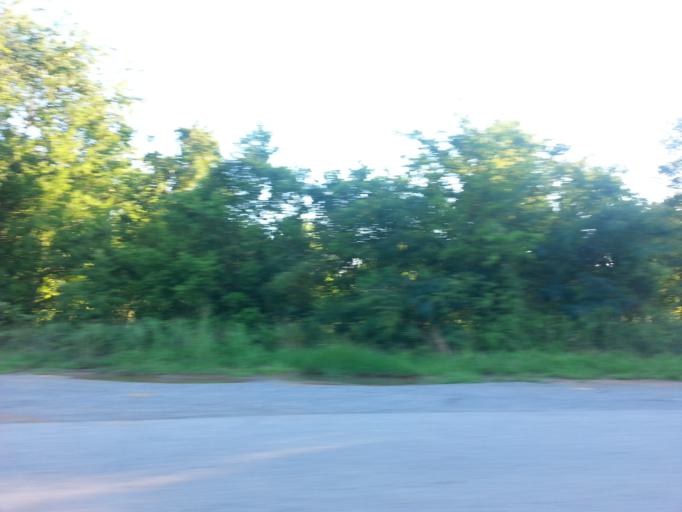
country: US
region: Tennessee
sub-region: Monroe County
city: Vonore
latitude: 35.6174
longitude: -84.1997
